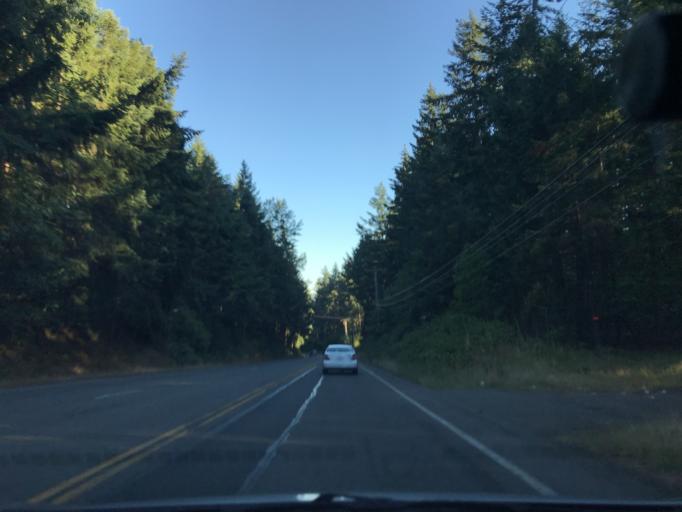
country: US
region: Washington
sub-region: Pierce County
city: Sumner
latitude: 47.2122
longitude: -122.2122
